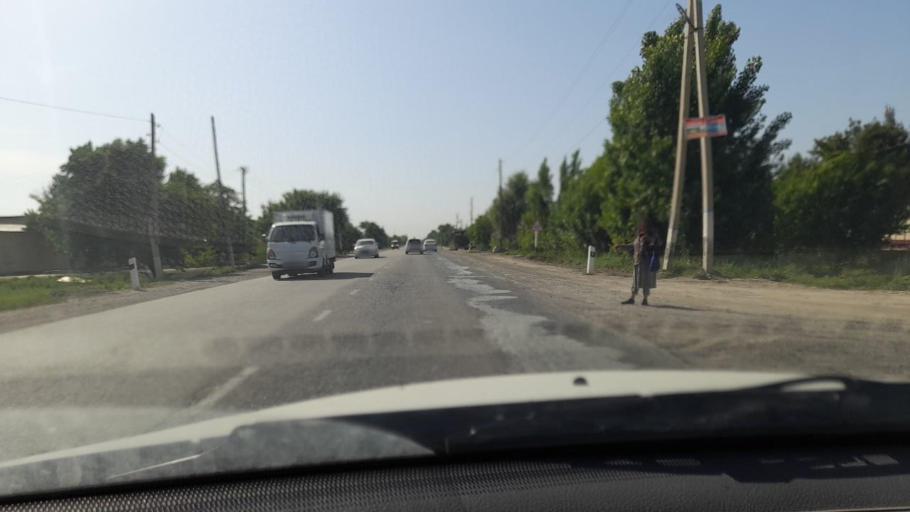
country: UZ
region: Bukhara
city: Romiton
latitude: 39.9101
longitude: 64.3963
